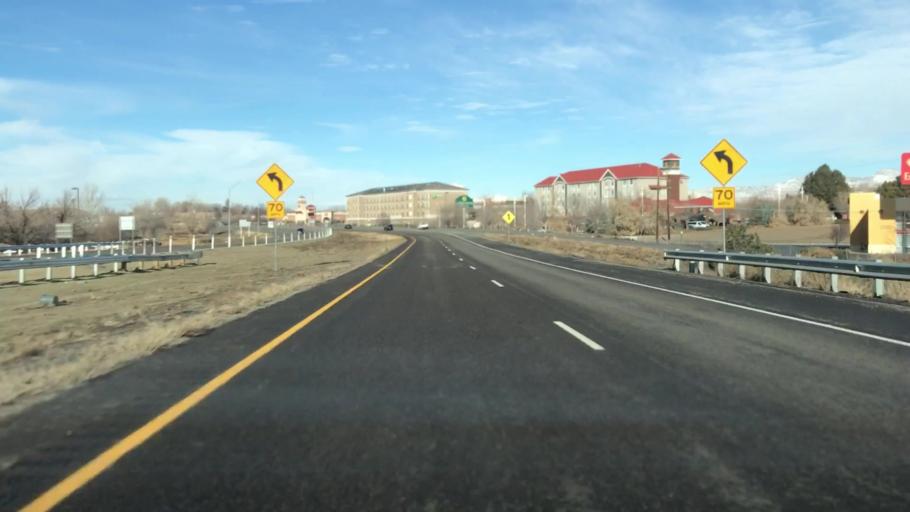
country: US
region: Colorado
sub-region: Mesa County
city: Grand Junction
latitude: 39.1124
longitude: -108.5402
